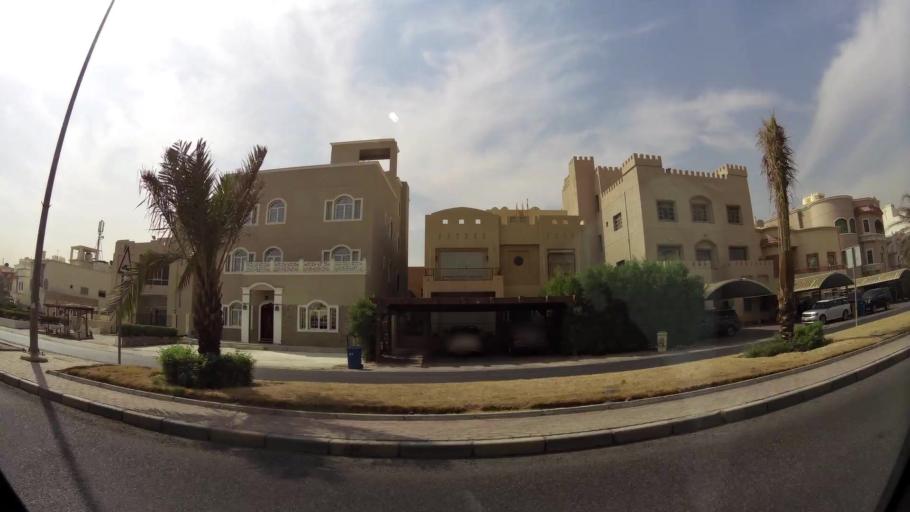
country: KW
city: Bayan
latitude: 29.2966
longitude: 48.0150
